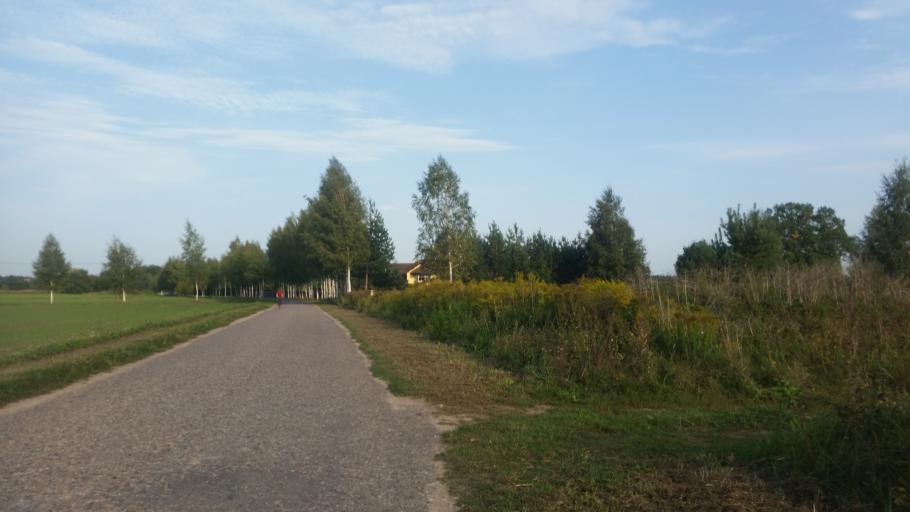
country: LV
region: Ikskile
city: Ikskile
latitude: 56.8172
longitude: 24.5438
